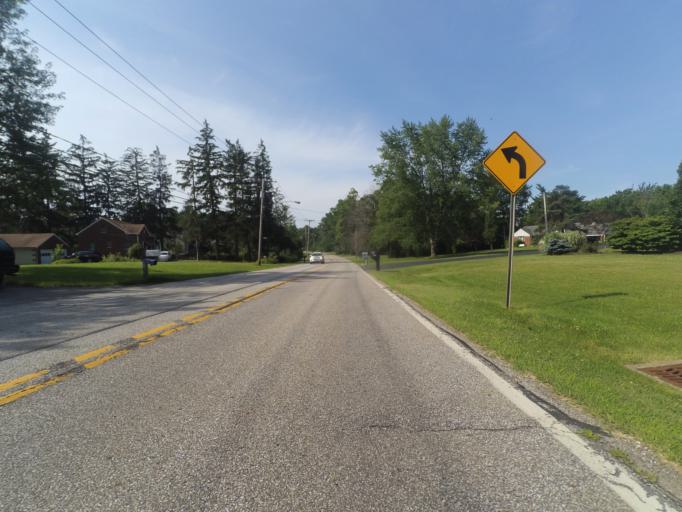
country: US
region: Ohio
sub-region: Cuyahoga County
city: Orange
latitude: 41.4219
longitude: -81.4820
